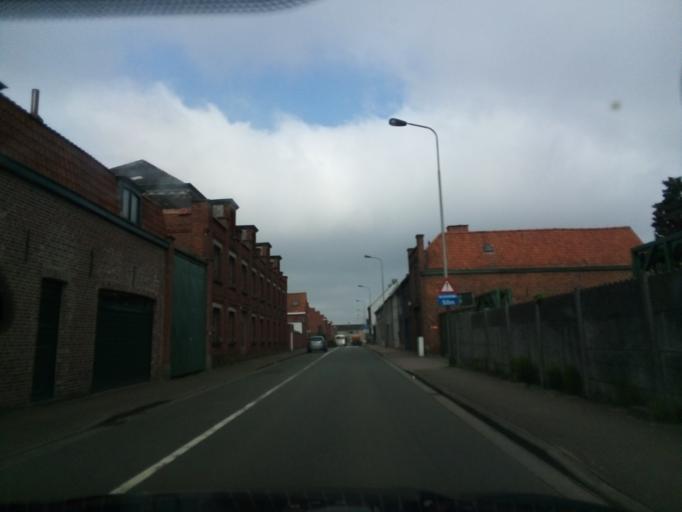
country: BE
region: Flanders
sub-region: Provincie West-Vlaanderen
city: Ingelmunster
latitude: 50.9227
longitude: 3.2527
